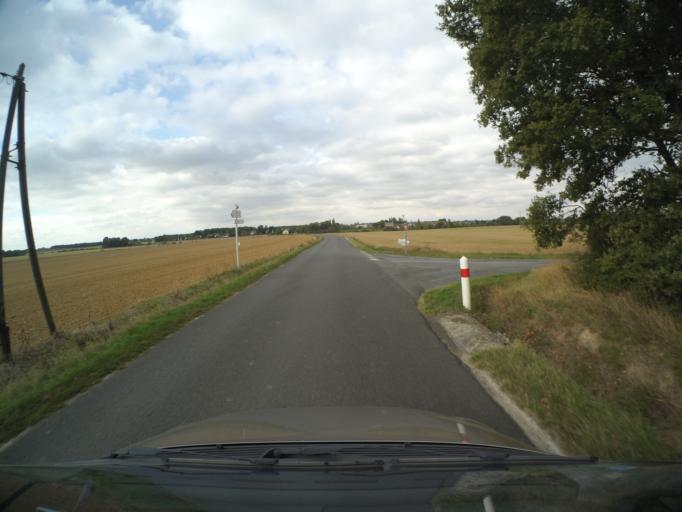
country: FR
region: Centre
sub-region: Departement d'Indre-et-Loire
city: Nazelles-Negron
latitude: 47.4812
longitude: 0.9503
